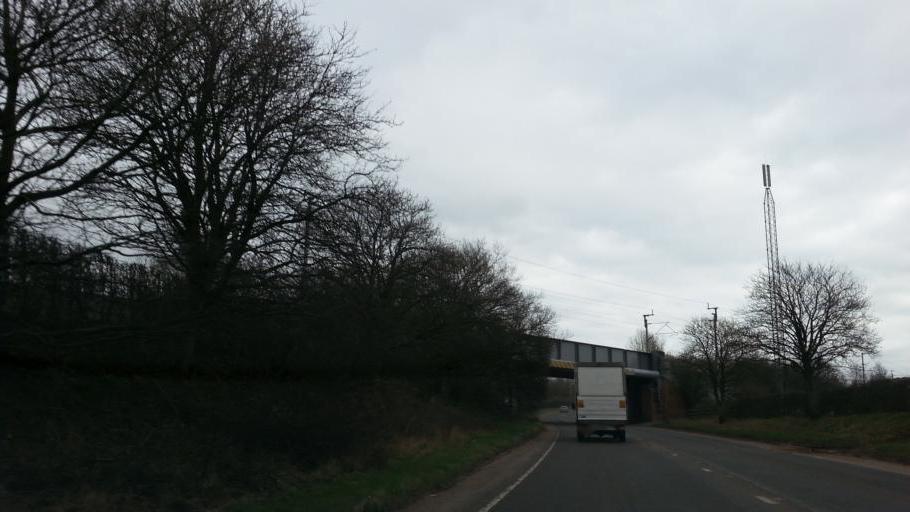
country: GB
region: England
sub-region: Staffordshire
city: Stone
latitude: 52.8799
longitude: -2.1124
